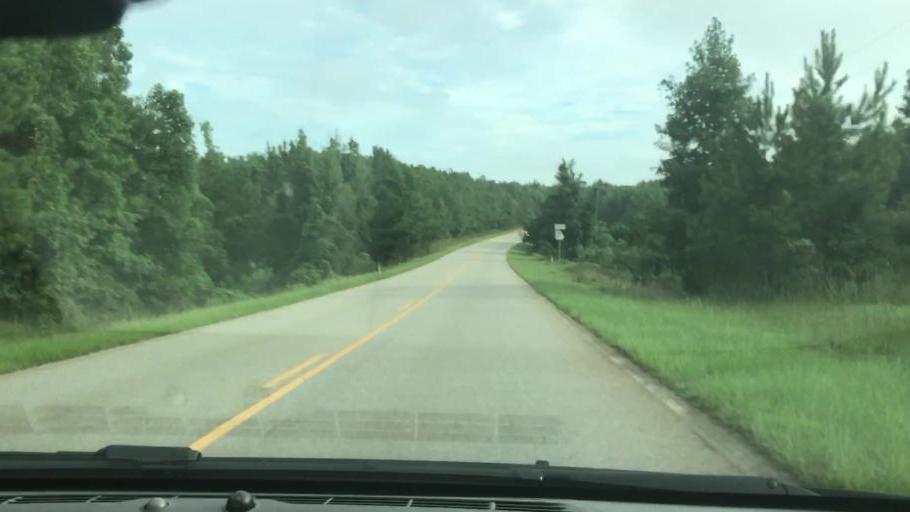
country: US
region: Georgia
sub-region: Stewart County
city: Lumpkin
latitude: 32.0130
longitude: -84.9313
